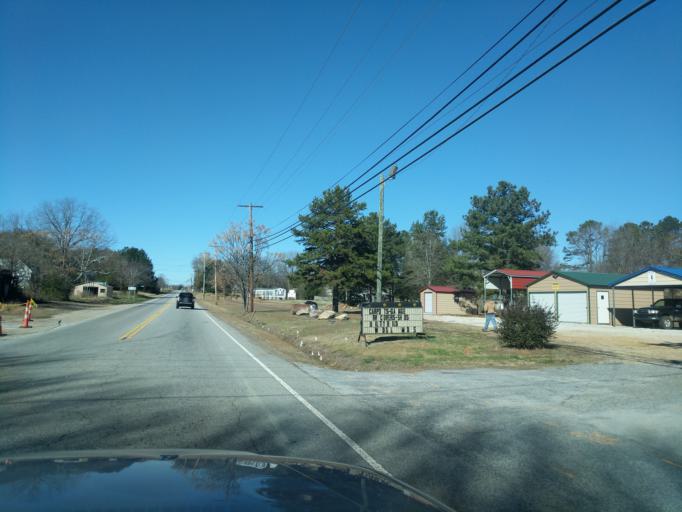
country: US
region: South Carolina
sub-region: Oconee County
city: Westminster
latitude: 34.6737
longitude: -83.1101
